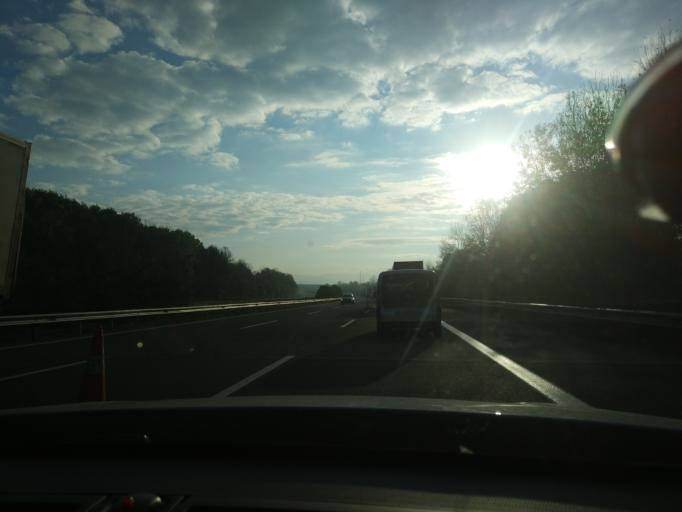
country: TR
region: Duzce
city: Duzce
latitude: 40.8107
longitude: 31.1225
